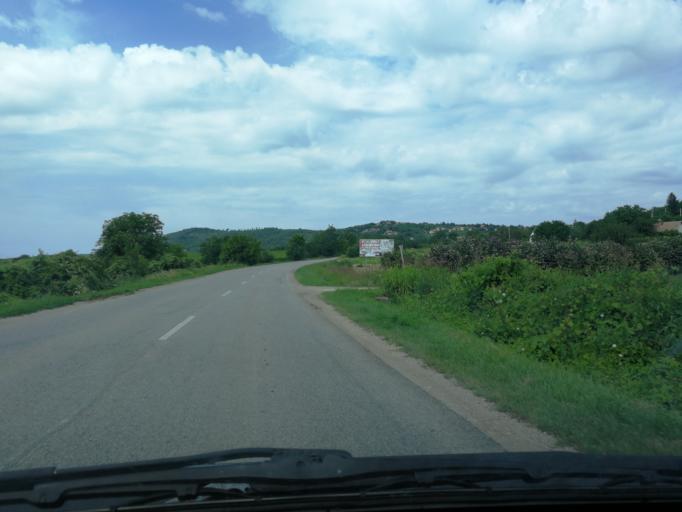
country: HU
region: Baranya
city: Harkany
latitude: 45.8764
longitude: 18.2452
